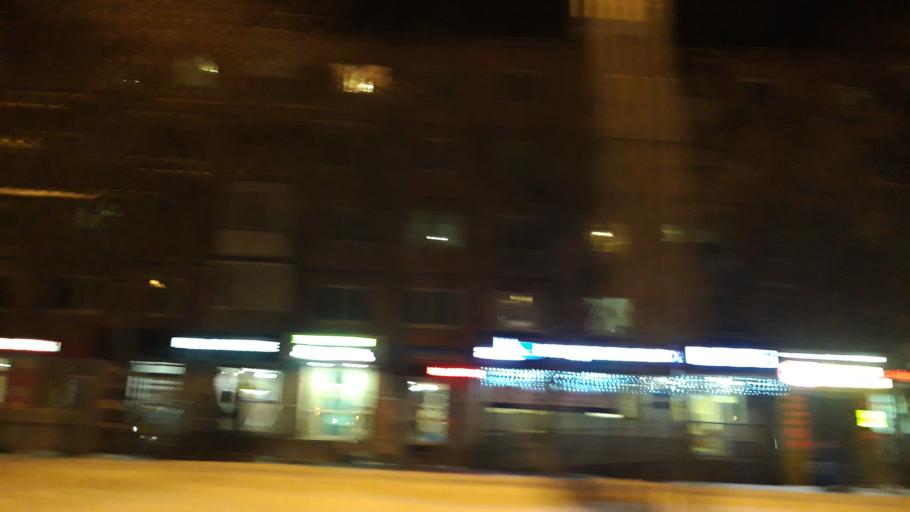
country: RU
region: Tjumen
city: Tyumen
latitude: 57.1590
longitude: 65.4883
